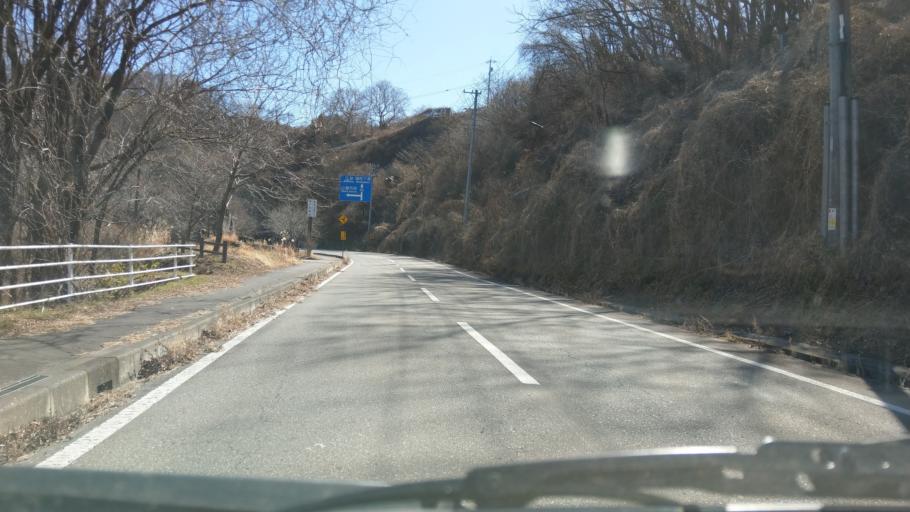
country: JP
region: Nagano
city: Komoro
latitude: 36.3298
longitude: 138.3945
